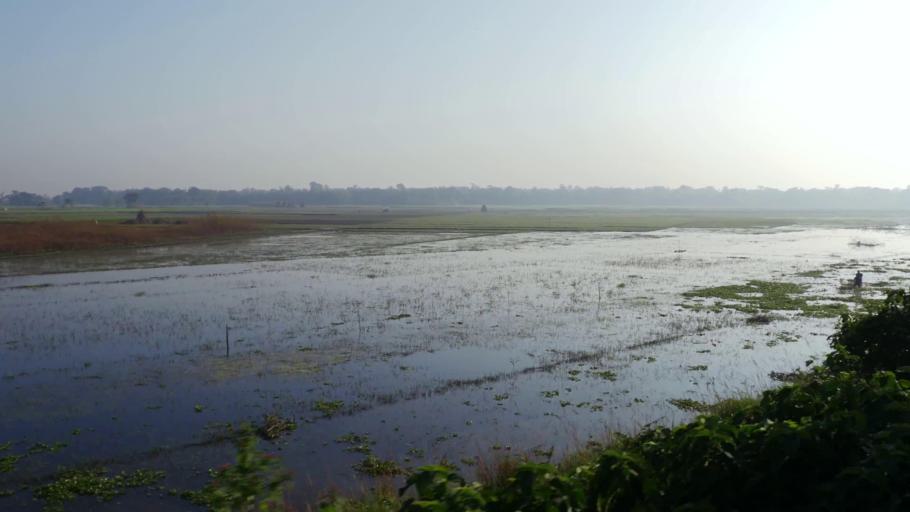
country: BD
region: Dhaka
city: Jamalpur
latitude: 24.9194
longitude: 89.9432
